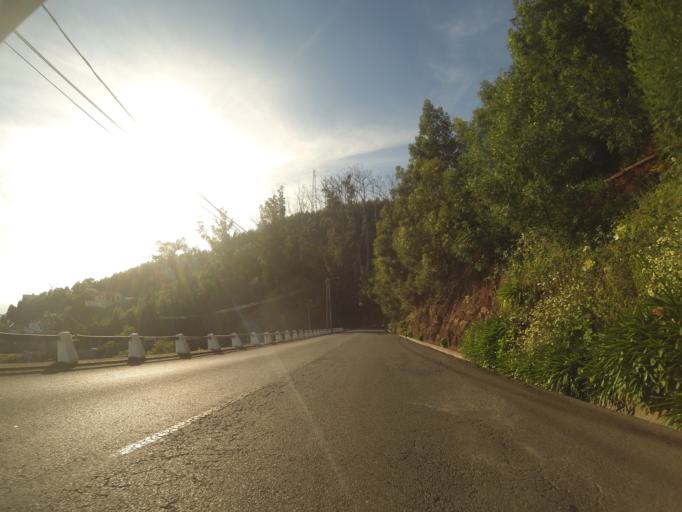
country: PT
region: Madeira
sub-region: Santa Cruz
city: Camacha
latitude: 32.6645
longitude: -16.8682
